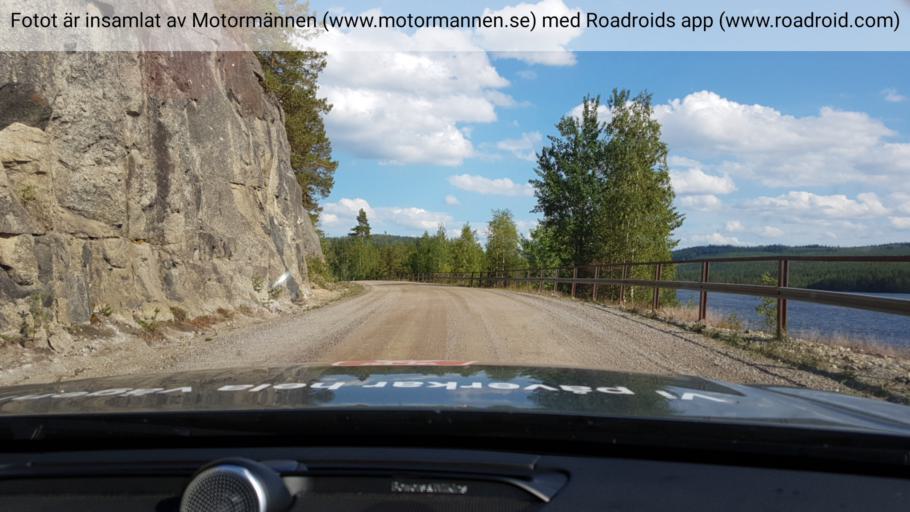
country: SE
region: Jaemtland
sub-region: Stroemsunds Kommun
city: Stroemsund
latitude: 63.9936
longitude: 15.9826
